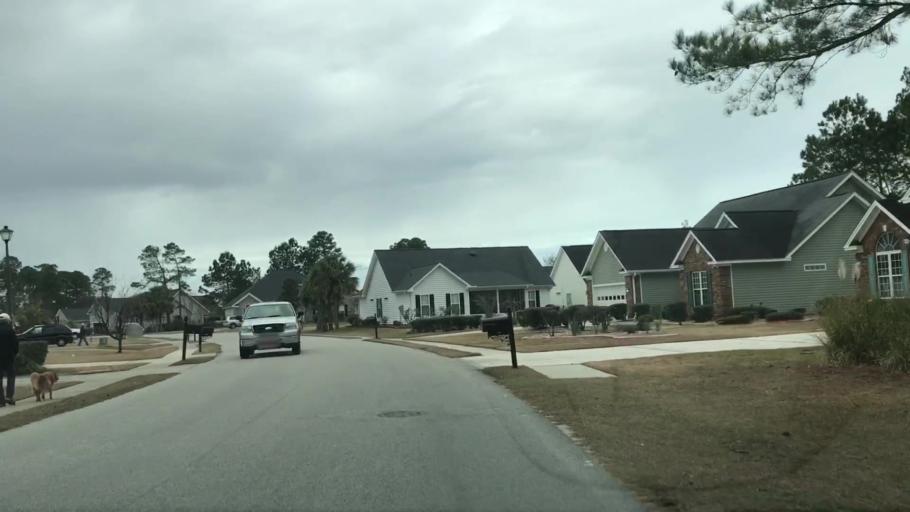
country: US
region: South Carolina
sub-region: Horry County
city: Red Hill
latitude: 33.7724
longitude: -79.0051
